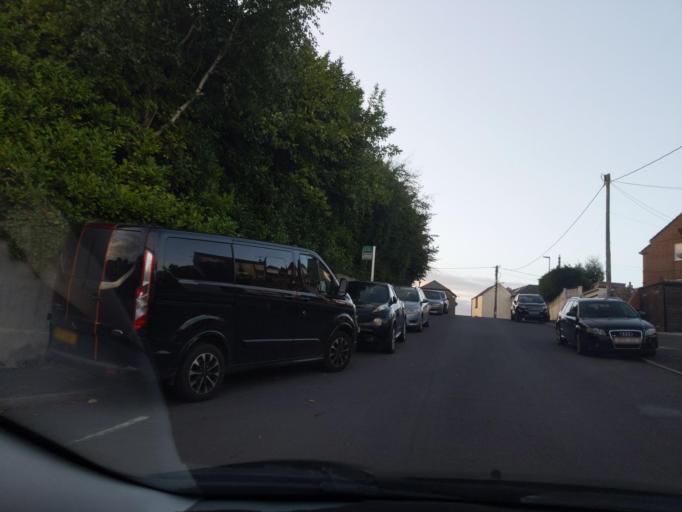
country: GB
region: England
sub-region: Plymouth
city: Plymstock
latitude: 50.3585
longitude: -4.0641
